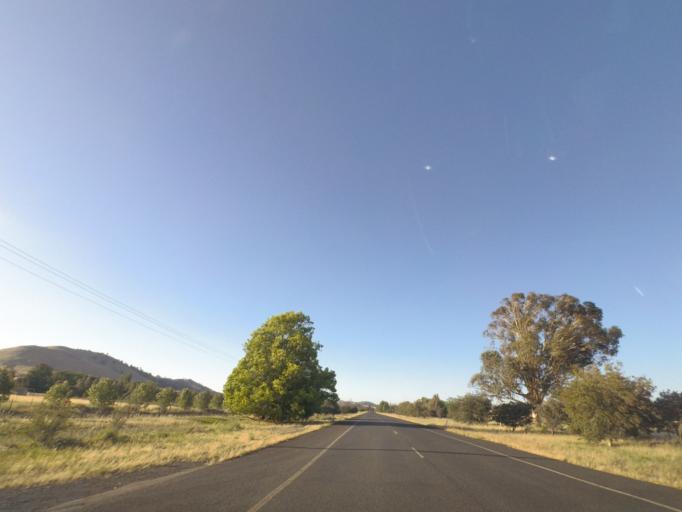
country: AU
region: New South Wales
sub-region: Gundagai
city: Gundagai
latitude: -34.9421
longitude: 148.1684
